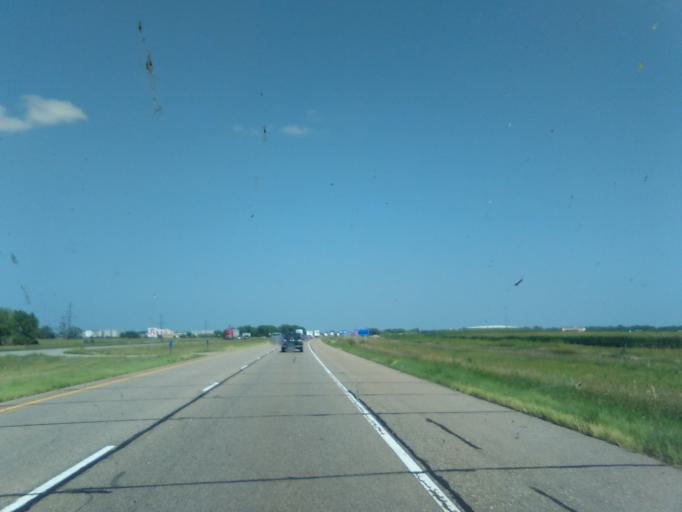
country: US
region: Nebraska
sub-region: Buffalo County
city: Kearney
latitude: 40.6703
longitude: -99.1077
